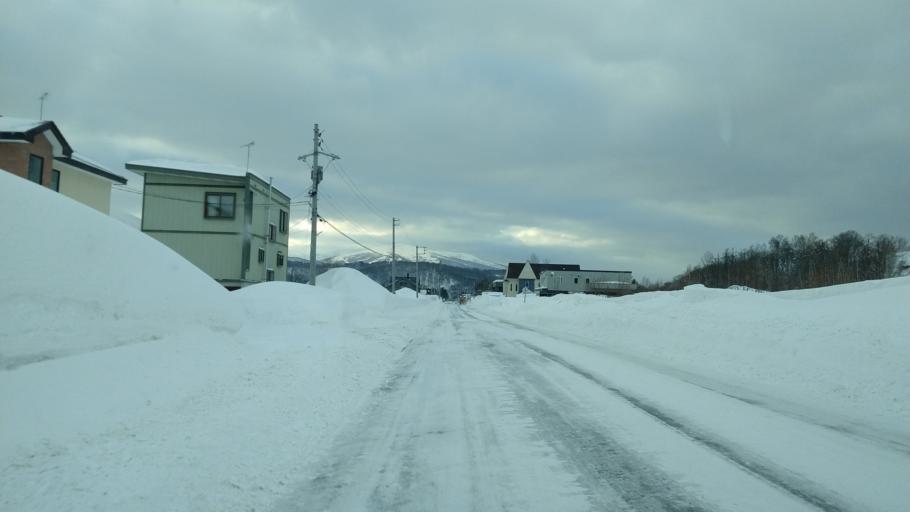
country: JP
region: Hokkaido
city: Niseko Town
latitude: 42.9084
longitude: 140.7648
